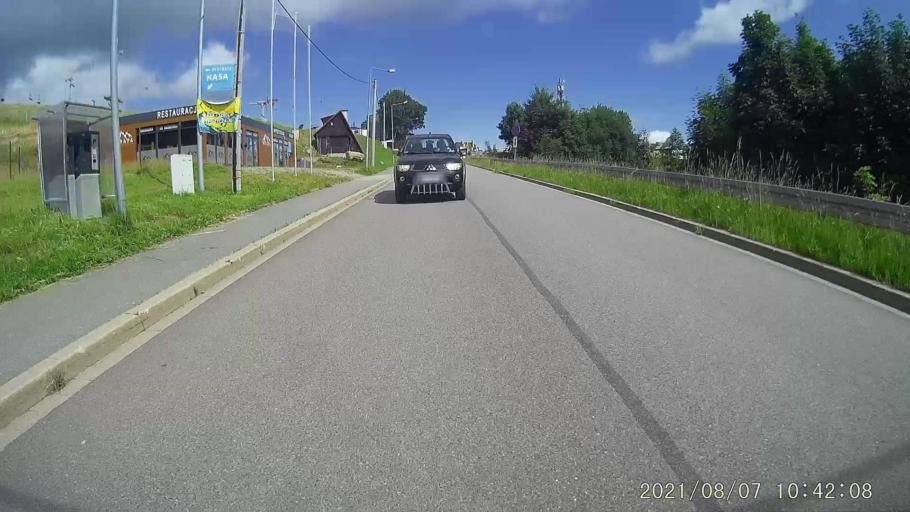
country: PL
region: Lower Silesian Voivodeship
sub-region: Powiat klodzki
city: Duszniki-Zdroj
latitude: 50.3337
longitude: 16.3893
